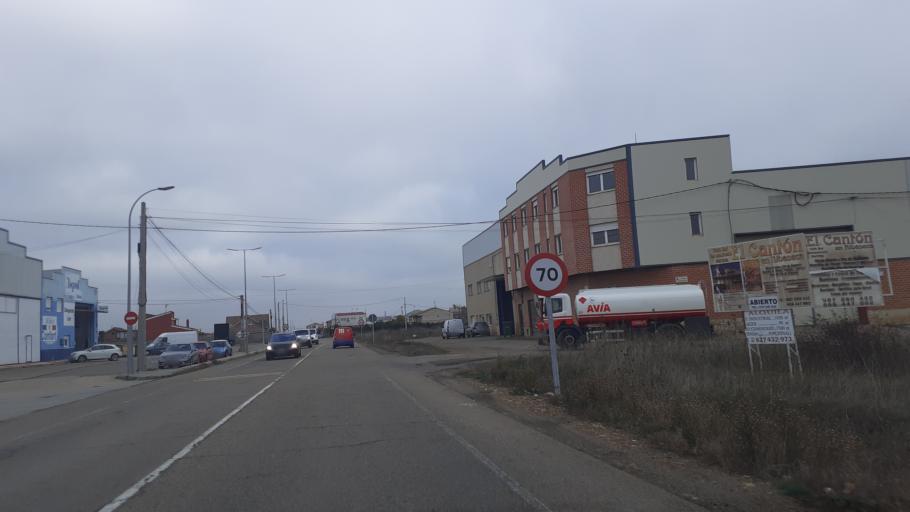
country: ES
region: Castille and Leon
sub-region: Provincia de Leon
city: Onzonilla
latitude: 42.5335
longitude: -5.5926
